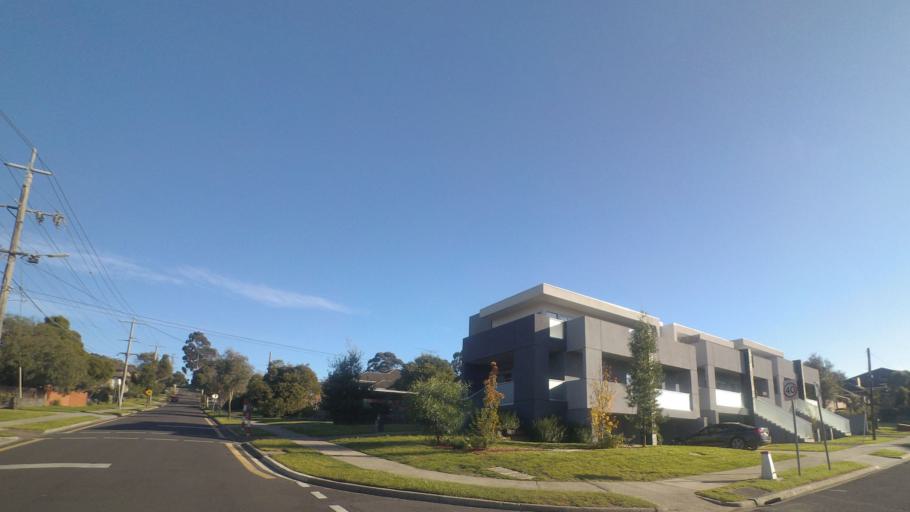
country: AU
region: Victoria
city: Macleod
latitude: -37.7358
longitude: 145.0626
